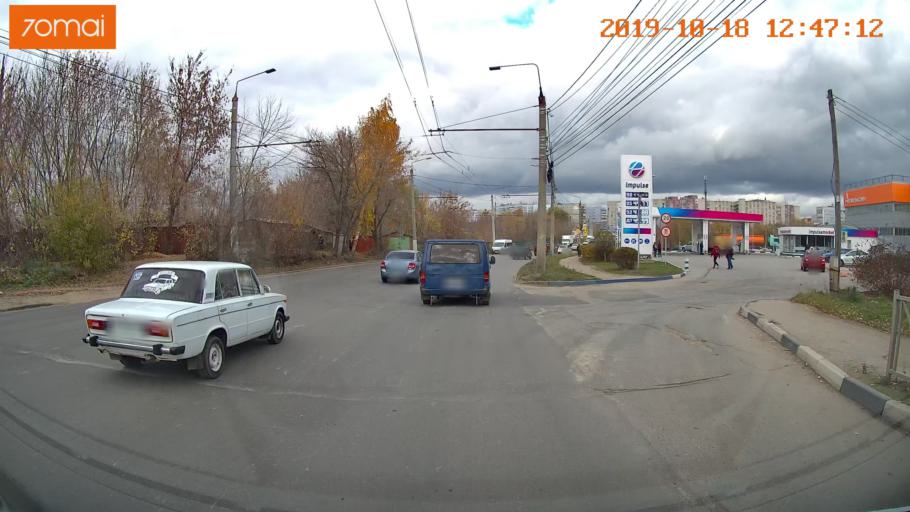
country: RU
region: Rjazan
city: Ryazan'
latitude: 54.6572
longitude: 39.6633
